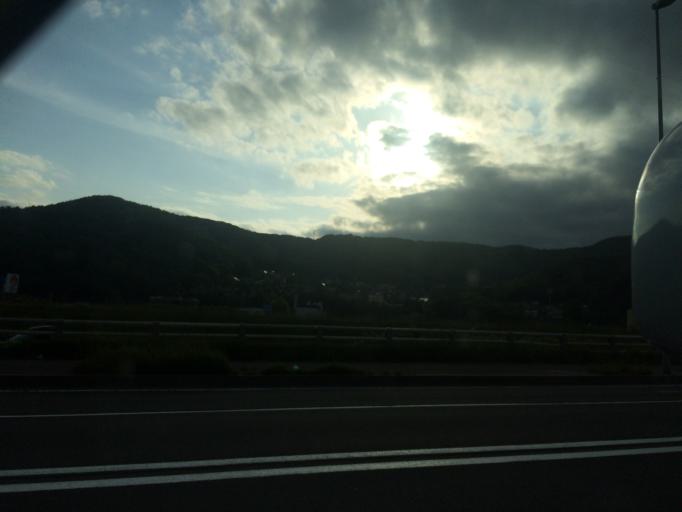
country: JP
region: Hokkaido
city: Sapporo
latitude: 43.0073
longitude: 141.3477
